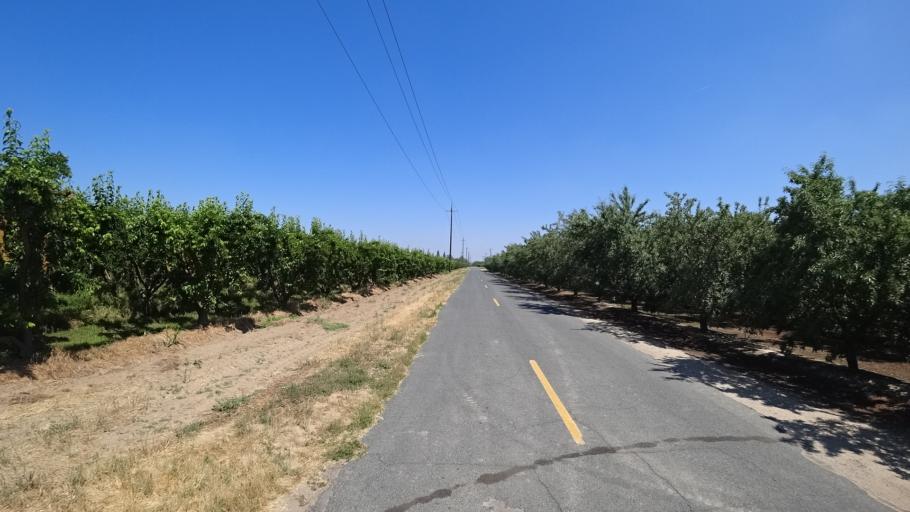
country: US
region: California
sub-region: Fresno County
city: Kingsburg
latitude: 36.4562
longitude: -119.5825
